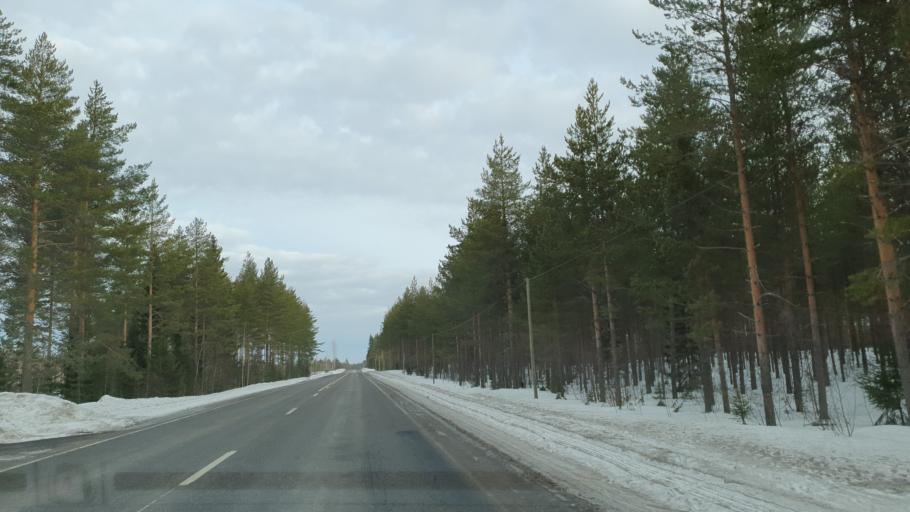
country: FI
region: Kainuu
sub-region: Kajaani
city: Vuokatti
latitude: 64.1849
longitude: 28.1860
